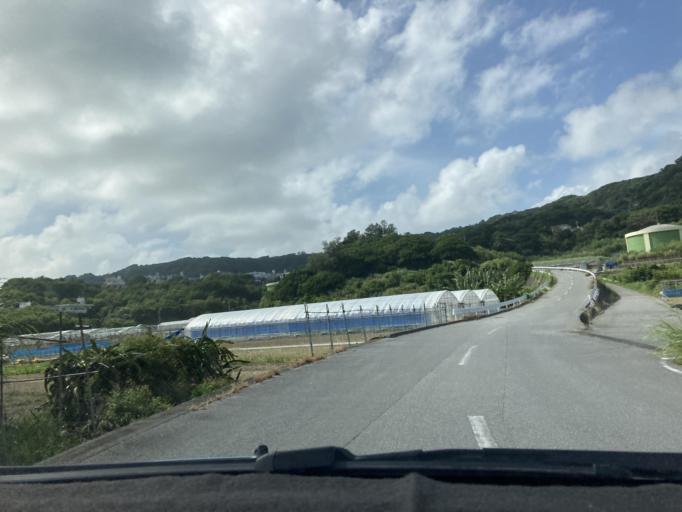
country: JP
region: Okinawa
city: Ginowan
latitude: 26.1519
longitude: 127.8061
